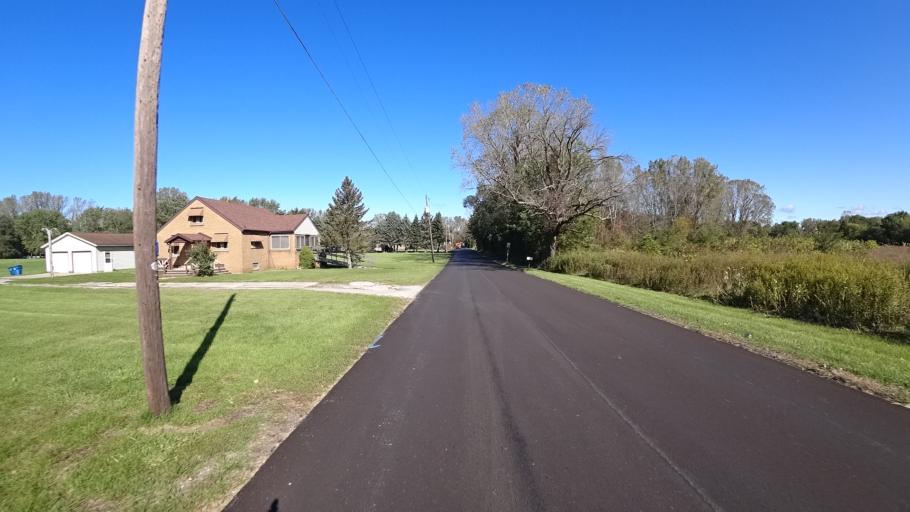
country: US
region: Indiana
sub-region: LaPorte County
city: Michigan City
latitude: 41.6916
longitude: -86.9131
